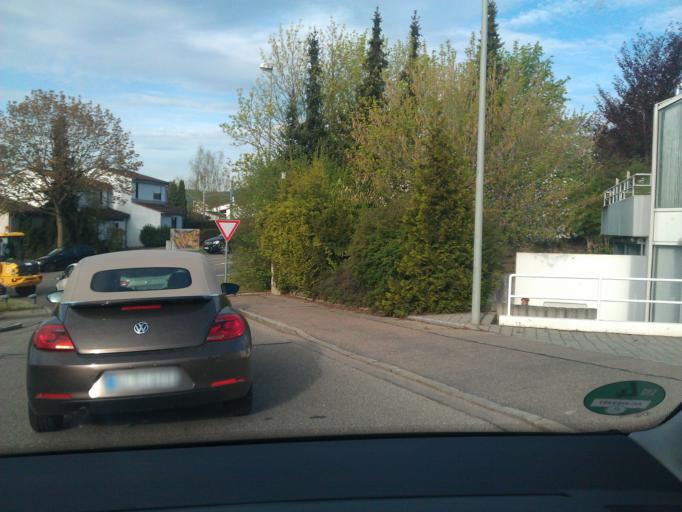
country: DE
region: Baden-Wuerttemberg
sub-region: Tuebingen Region
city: Ulm
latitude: 48.4098
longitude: 9.9487
